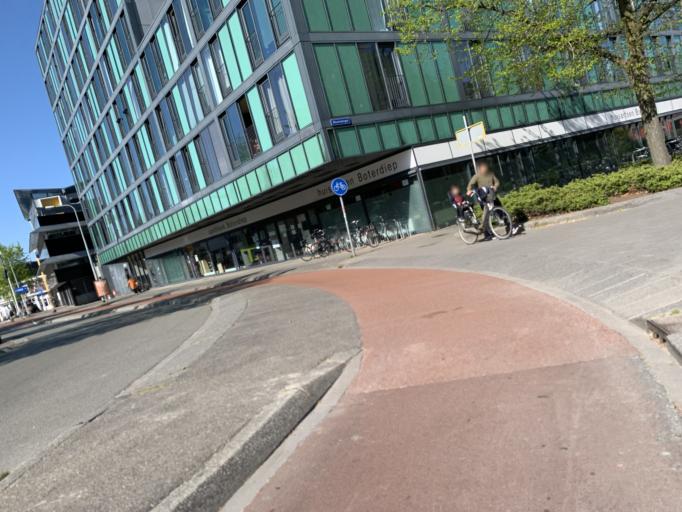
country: NL
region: Groningen
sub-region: Gemeente Groningen
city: Groningen
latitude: 53.2261
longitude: 6.5619
